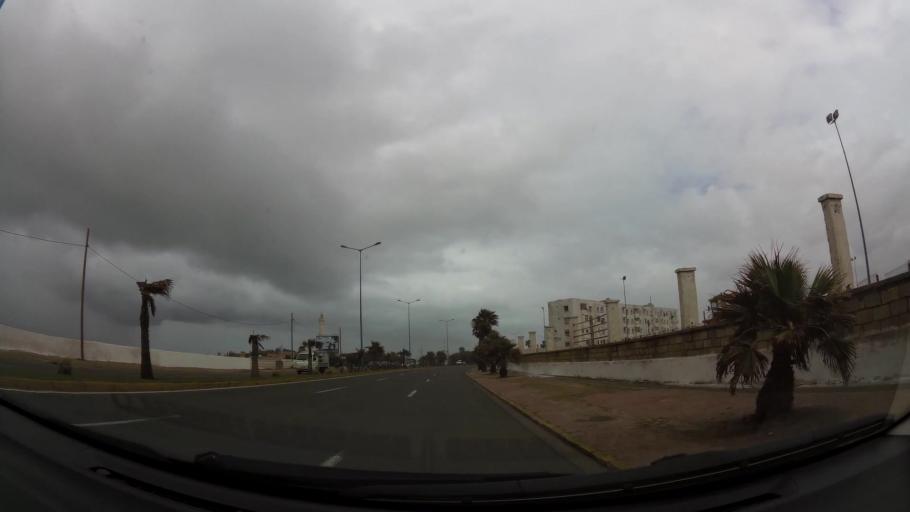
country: MA
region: Grand Casablanca
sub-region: Casablanca
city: Casablanca
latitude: 33.6060
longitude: -7.6571
